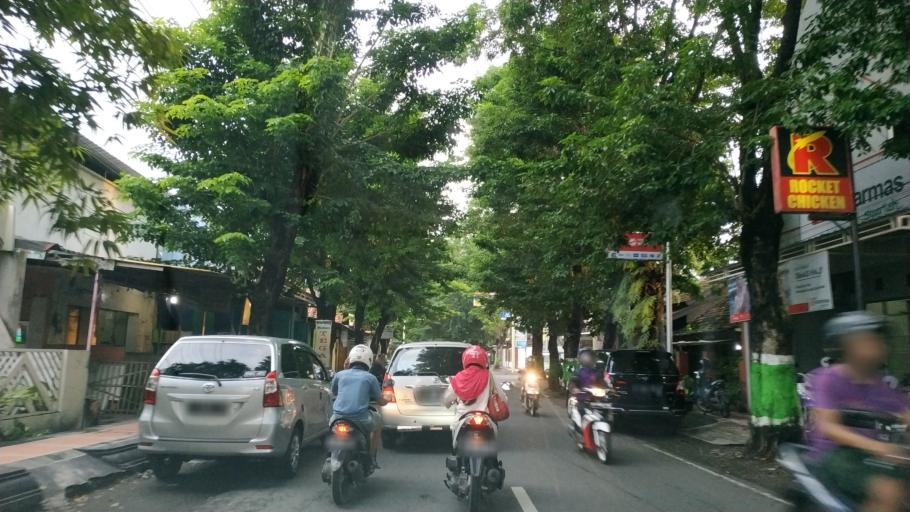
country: ID
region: Central Java
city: Kudus
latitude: -6.8099
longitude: 110.8546
